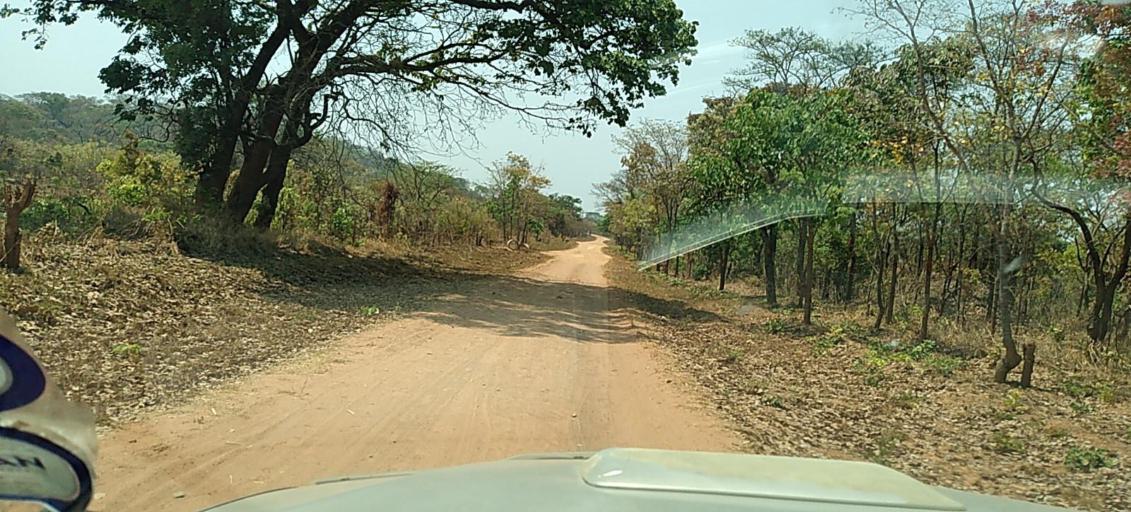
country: ZM
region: North-Western
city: Kasempa
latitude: -13.5508
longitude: 26.0209
